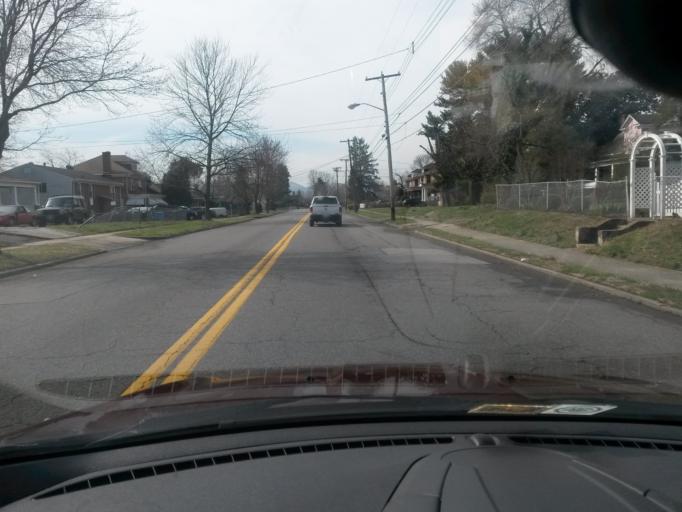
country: US
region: Virginia
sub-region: City of Roanoke
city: Roanoke
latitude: 37.2964
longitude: -79.9729
